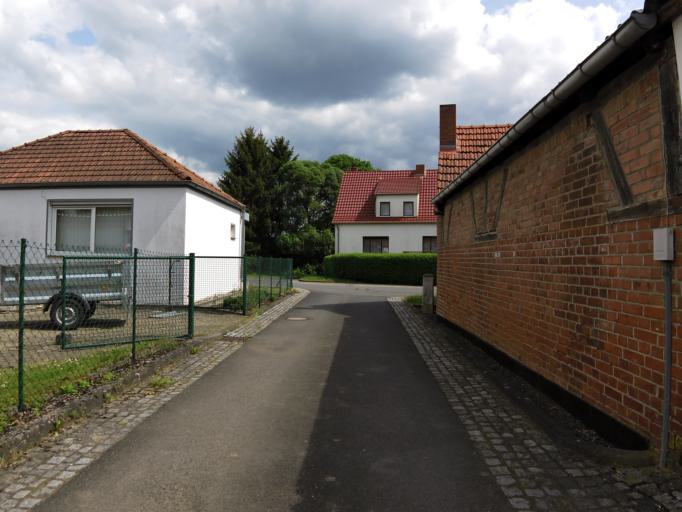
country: DE
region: Thuringia
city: Ifta
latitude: 51.0637
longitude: 10.1770
